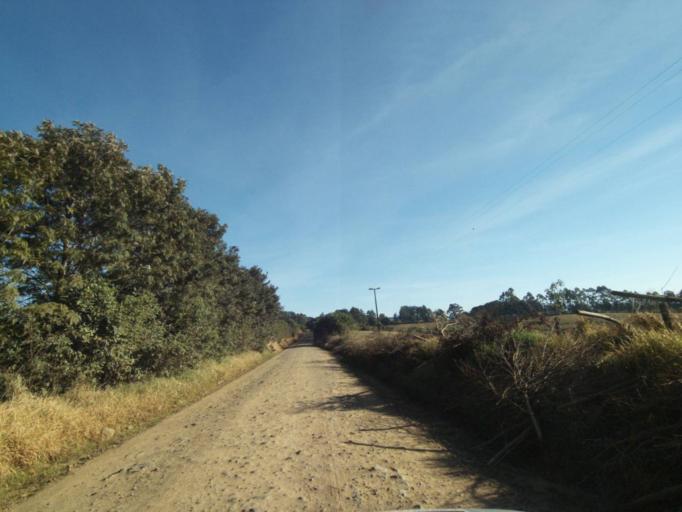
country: BR
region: Parana
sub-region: Tibagi
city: Tibagi
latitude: -24.5447
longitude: -50.6167
